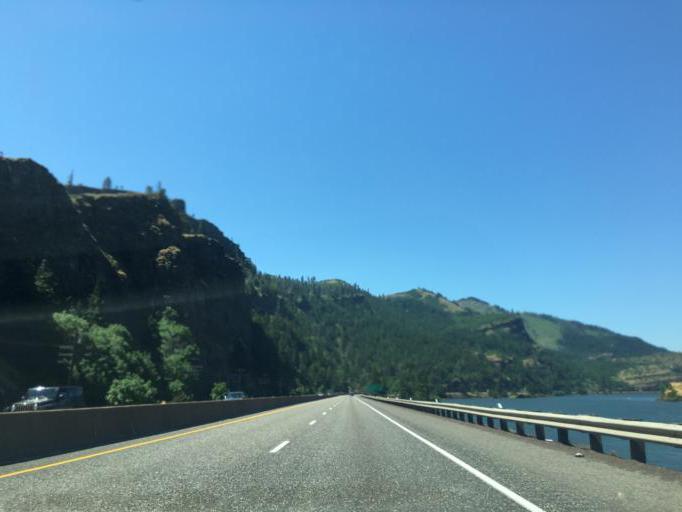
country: US
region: Washington
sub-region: Klickitat County
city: White Salmon
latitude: 45.6873
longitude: -121.4140
